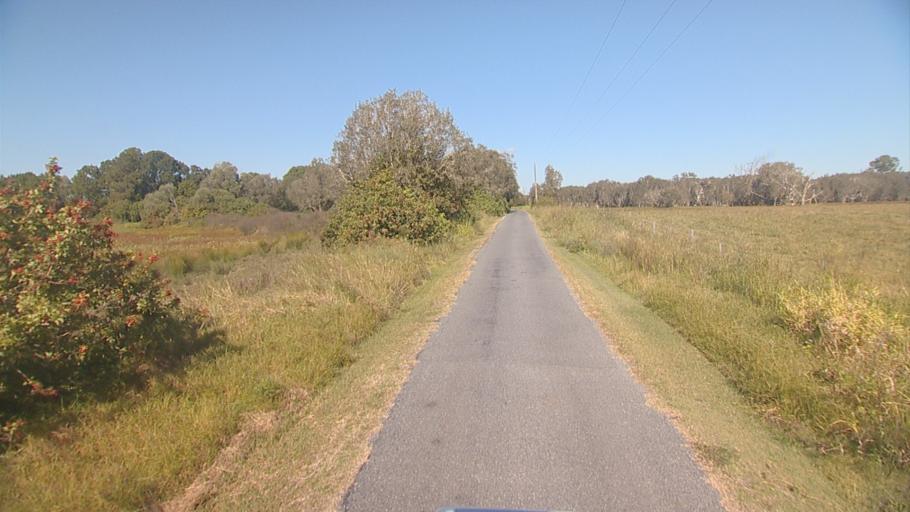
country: AU
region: Queensland
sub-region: Gold Coast
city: Yatala
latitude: -27.6838
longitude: 153.2250
